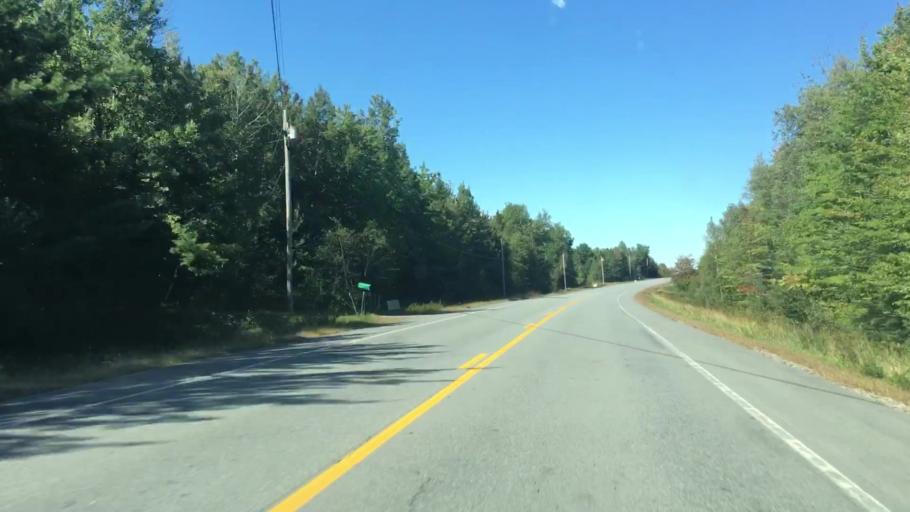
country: US
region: Maine
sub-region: Piscataquis County
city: Sangerville
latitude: 45.0684
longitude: -69.4588
